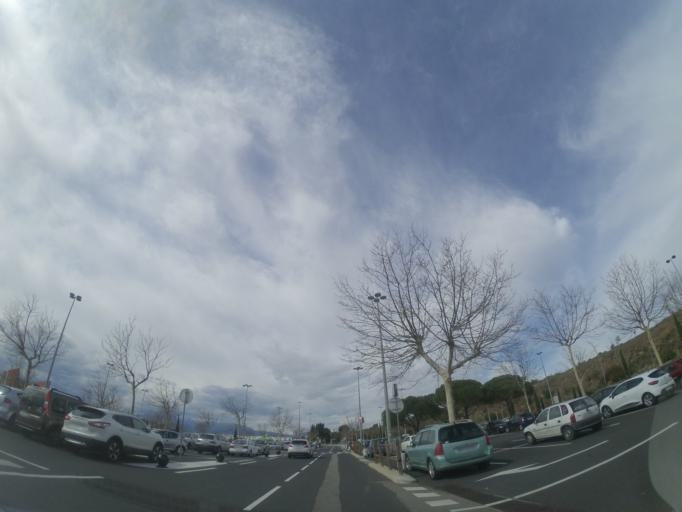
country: FR
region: Languedoc-Roussillon
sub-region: Departement des Pyrenees-Orientales
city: Pollestres
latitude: 42.6703
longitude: 2.8811
